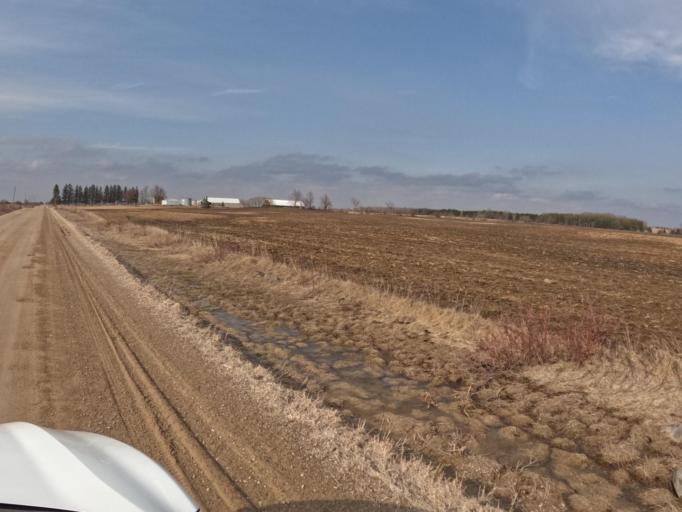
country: CA
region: Ontario
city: Orangeville
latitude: 43.9104
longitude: -80.2872
